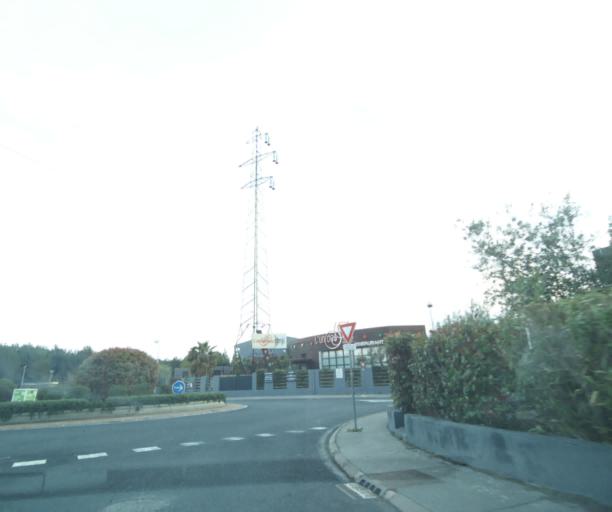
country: FR
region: Languedoc-Roussillon
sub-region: Departement de l'Herault
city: Saint-Jean-de-Vedas
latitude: 43.5683
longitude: 3.8390
